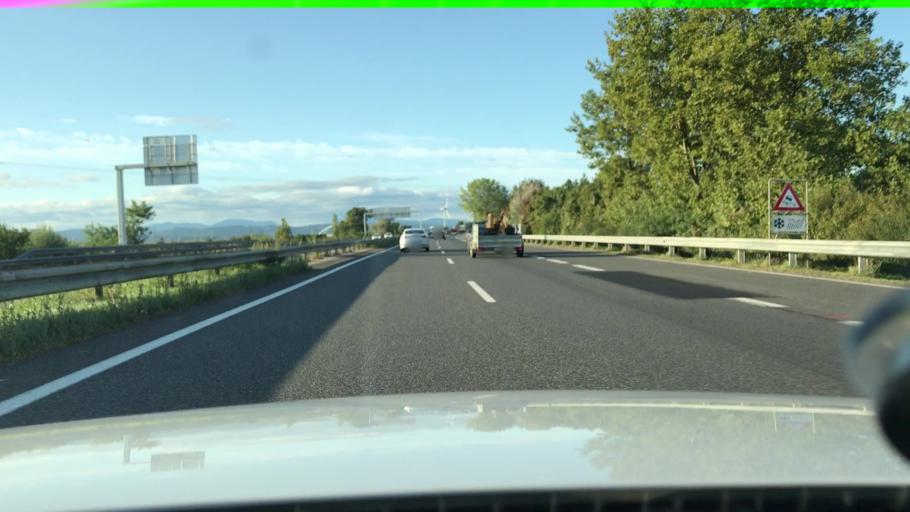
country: AT
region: Lower Austria
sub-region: Sankt Polten Stadt
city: Sankt Poelten
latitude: 48.2276
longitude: 15.6803
